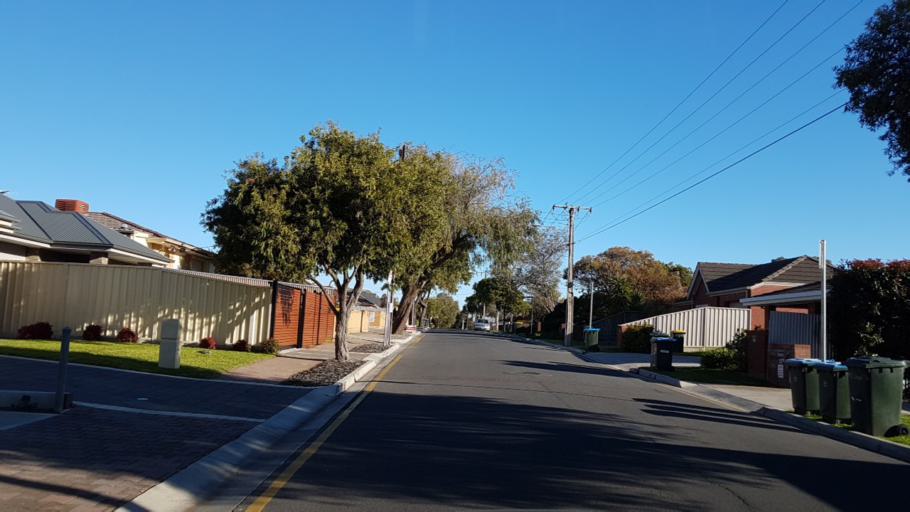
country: AU
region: South Australia
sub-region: Campbelltown
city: Campbelltown
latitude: -34.8782
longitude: 138.6609
